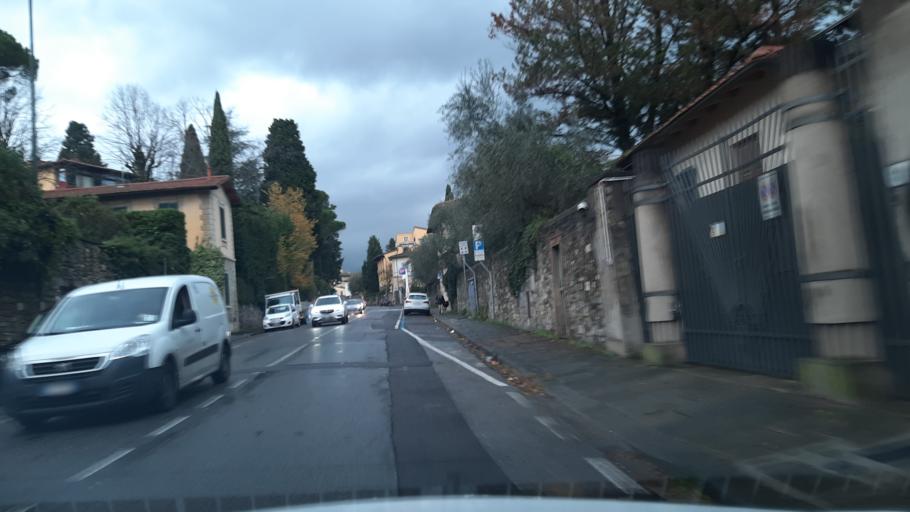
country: IT
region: Tuscany
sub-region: Province of Florence
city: Florence
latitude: 43.7928
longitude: 11.2614
